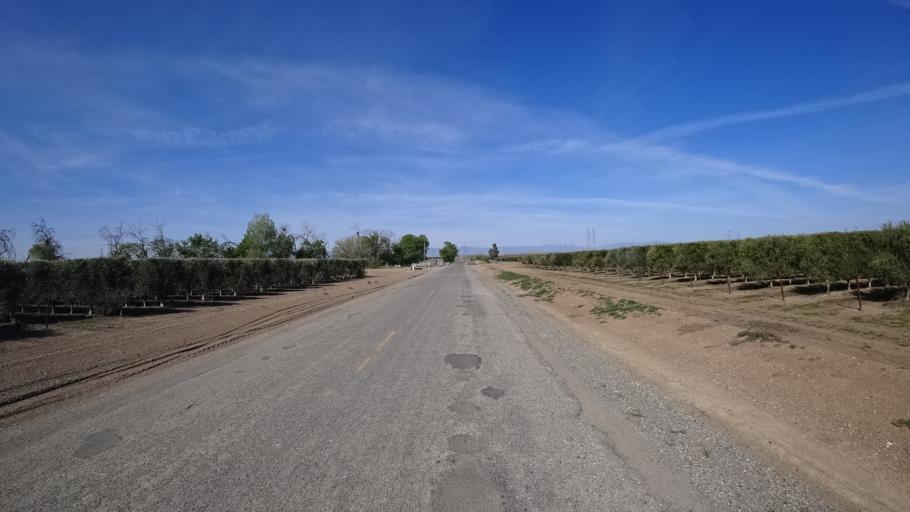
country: US
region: California
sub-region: Glenn County
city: Willows
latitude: 39.6116
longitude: -122.2591
